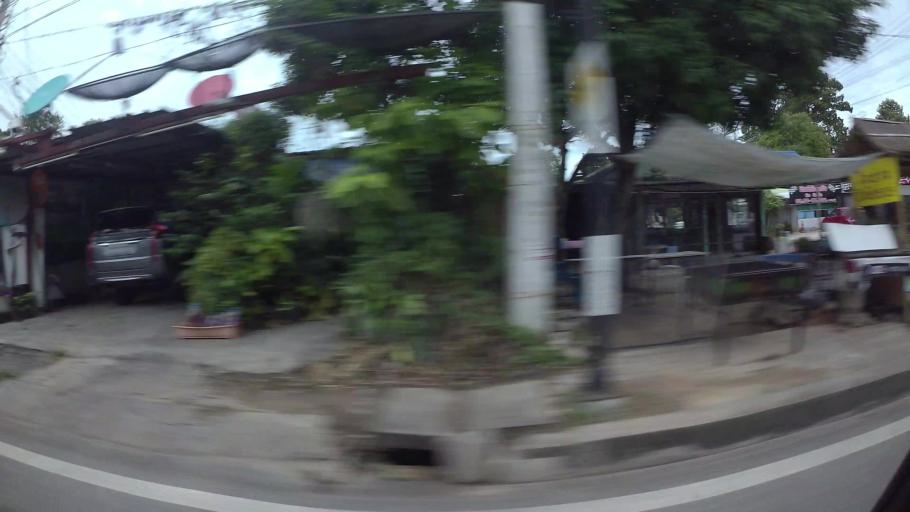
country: TH
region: Chon Buri
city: Si Racha
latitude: 13.1220
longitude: 100.9449
